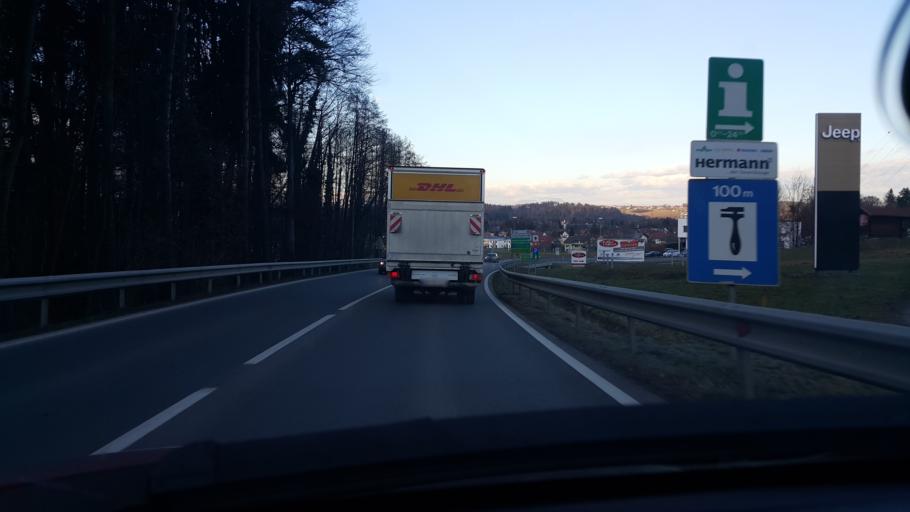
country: AT
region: Styria
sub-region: Politischer Bezirk Deutschlandsberg
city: Deutschlandsberg
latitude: 46.8104
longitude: 15.2273
